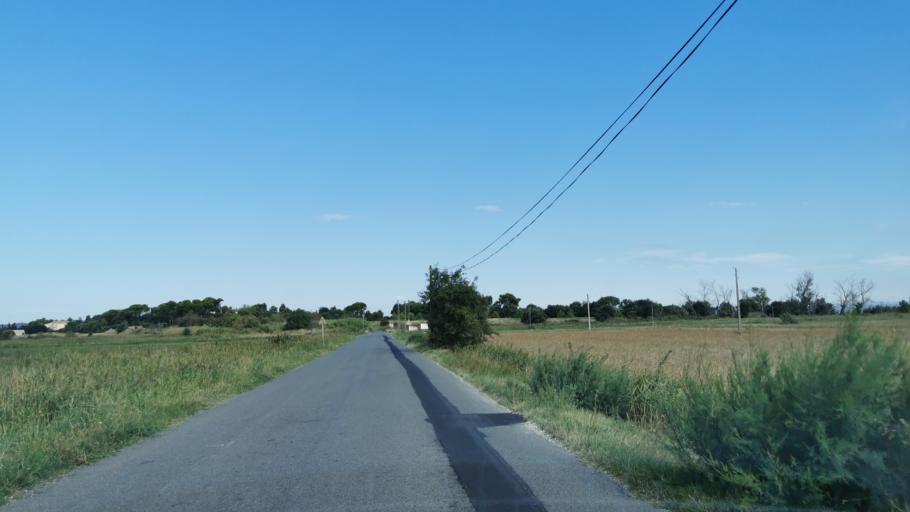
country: FR
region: Languedoc-Roussillon
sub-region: Departement de l'Aude
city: Narbonne
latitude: 43.1406
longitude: 3.0268
